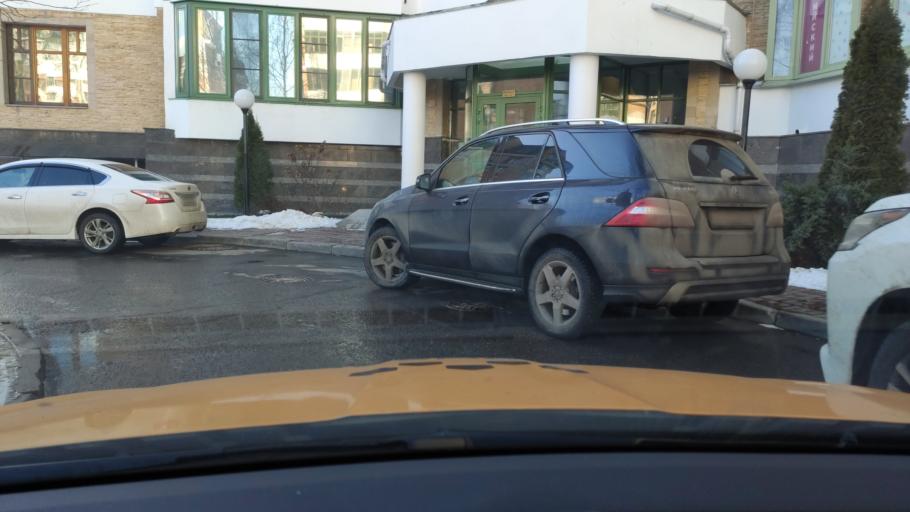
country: RU
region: Moscow
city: Rublevo
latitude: 55.7705
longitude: 37.3968
